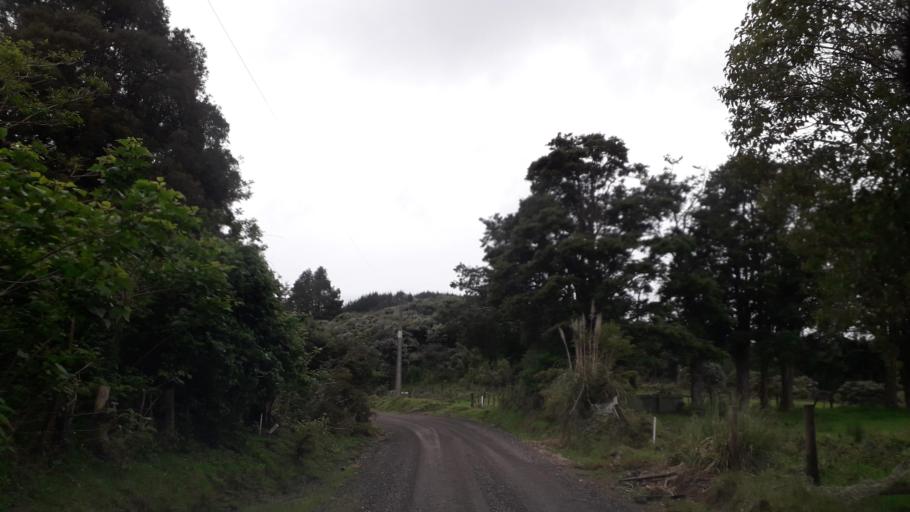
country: NZ
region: Northland
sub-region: Far North District
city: Kaitaia
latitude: -35.3771
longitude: 173.4113
